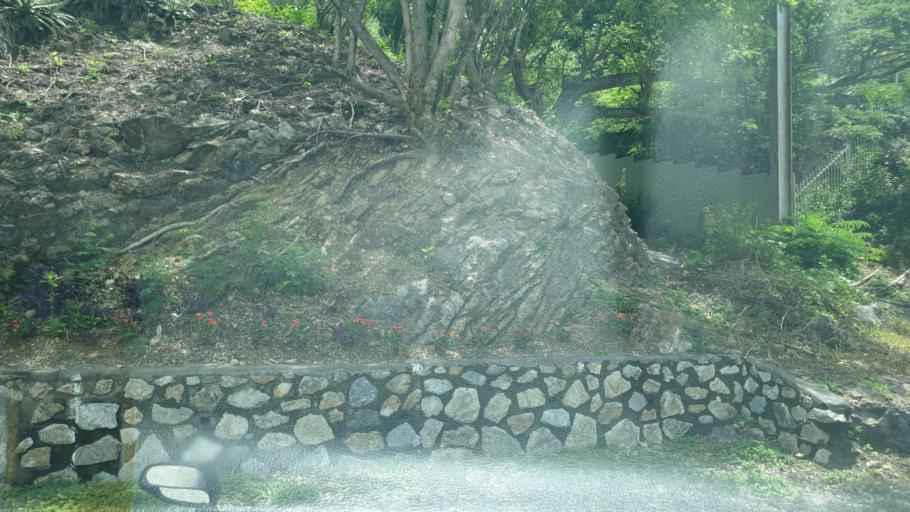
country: PG
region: National Capital
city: Port Moresby
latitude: -9.4733
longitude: 147.1569
